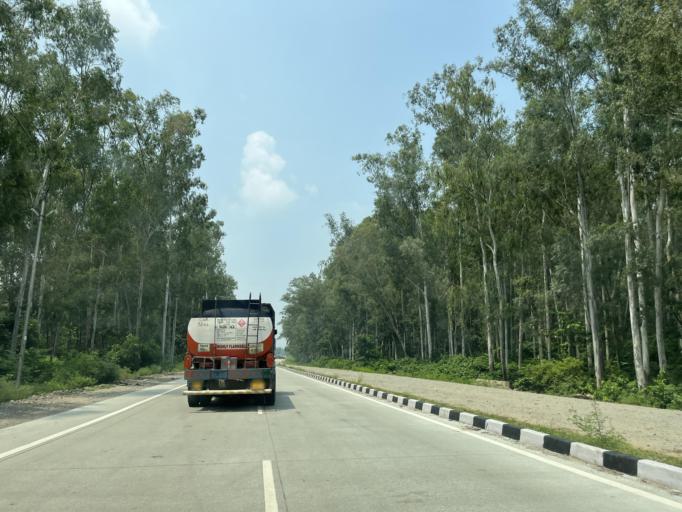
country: IN
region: Uttarakhand
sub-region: Haridwar
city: Sultanpur
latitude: 29.8345
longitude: 78.1990
